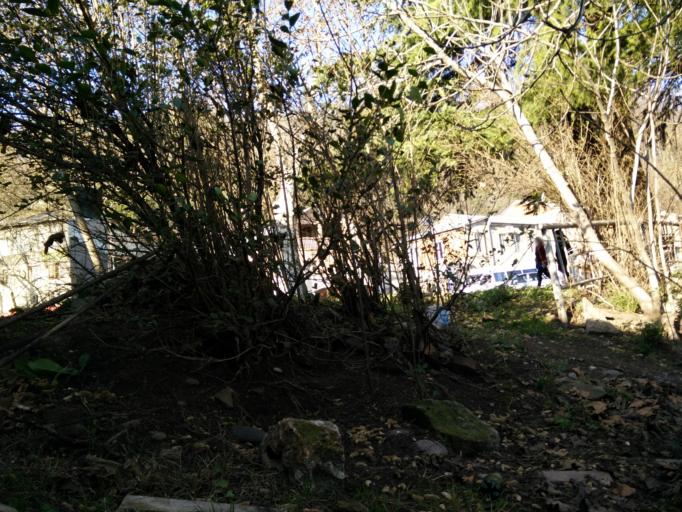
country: GE
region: Imereti
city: Kutaisi
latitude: 42.2698
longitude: 42.6987
